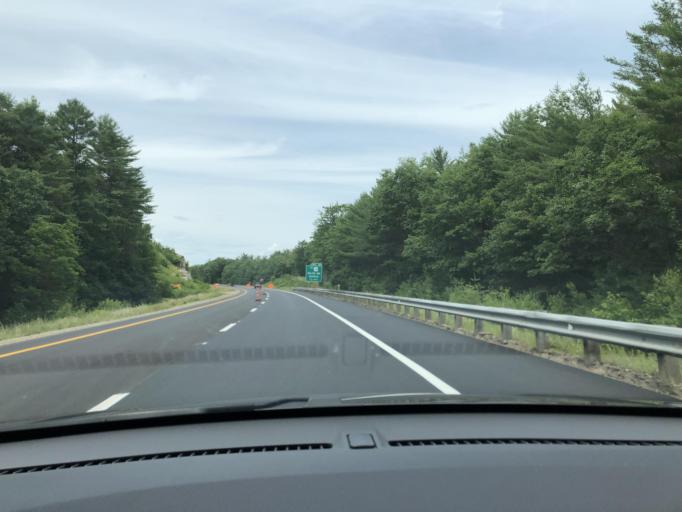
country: US
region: New Hampshire
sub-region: Merrimack County
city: Sutton
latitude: 43.3463
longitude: -71.9093
